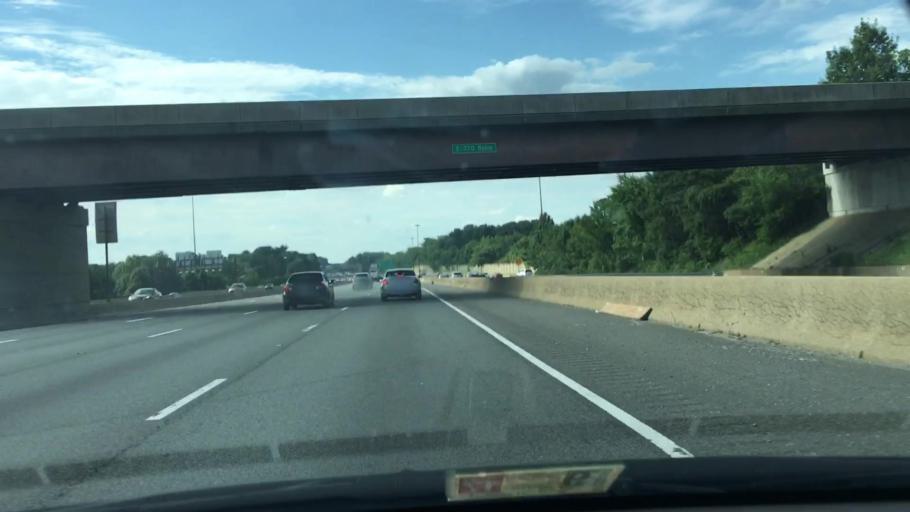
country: US
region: Maryland
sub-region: Montgomery County
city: Gaithersburg
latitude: 39.1221
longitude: -77.1986
